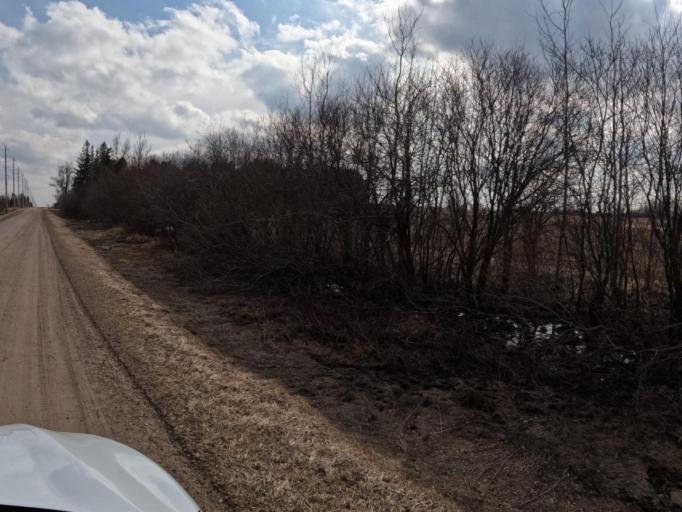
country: CA
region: Ontario
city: Shelburne
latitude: 43.9776
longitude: -80.3030
